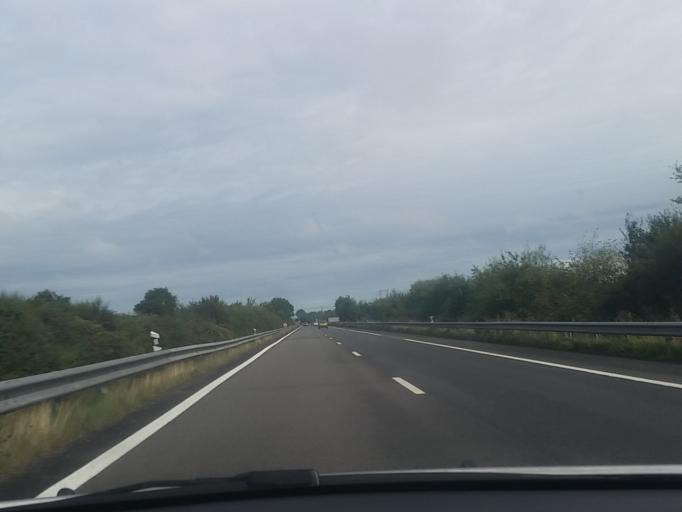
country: FR
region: Pays de la Loire
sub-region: Departement de la Loire-Atlantique
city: La Grigonnais
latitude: 47.5051
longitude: -1.6388
